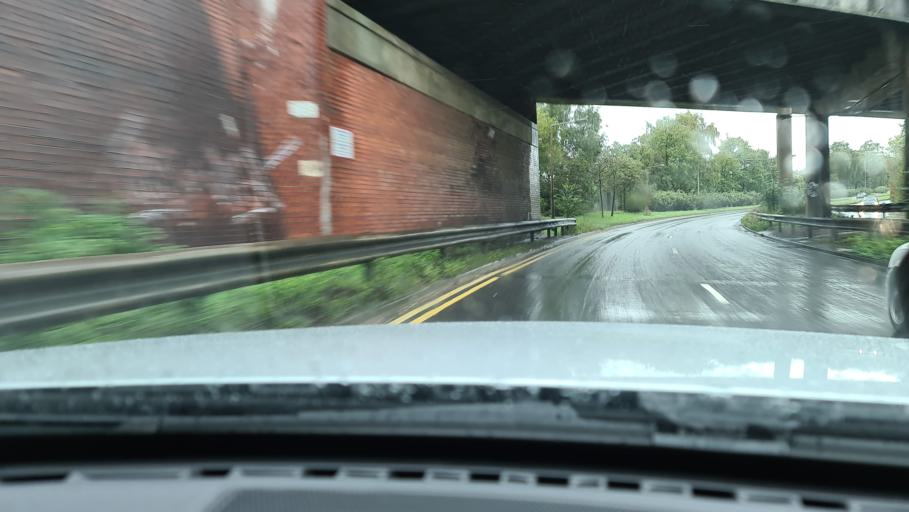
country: GB
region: England
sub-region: Buckinghamshire
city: Bletchley
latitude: 52.0007
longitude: -0.7275
